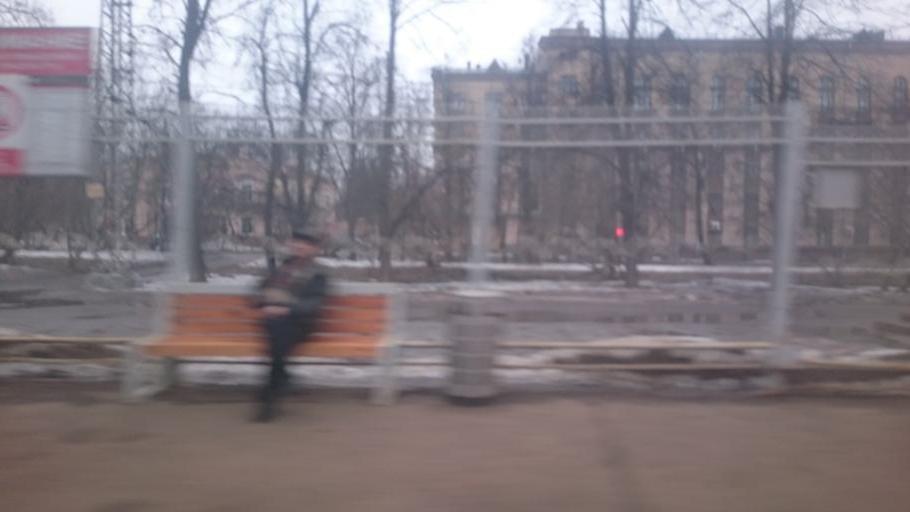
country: RU
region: Moscow
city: Pokrovskoye-Streshnevo
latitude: 55.8265
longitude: 37.4423
